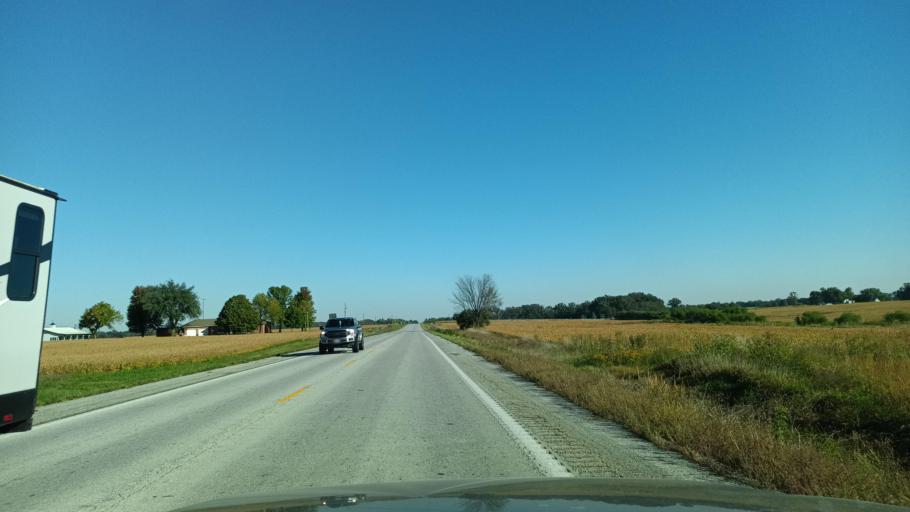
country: US
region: Missouri
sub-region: Audrain County
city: Vandalia
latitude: 39.2899
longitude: -91.6440
